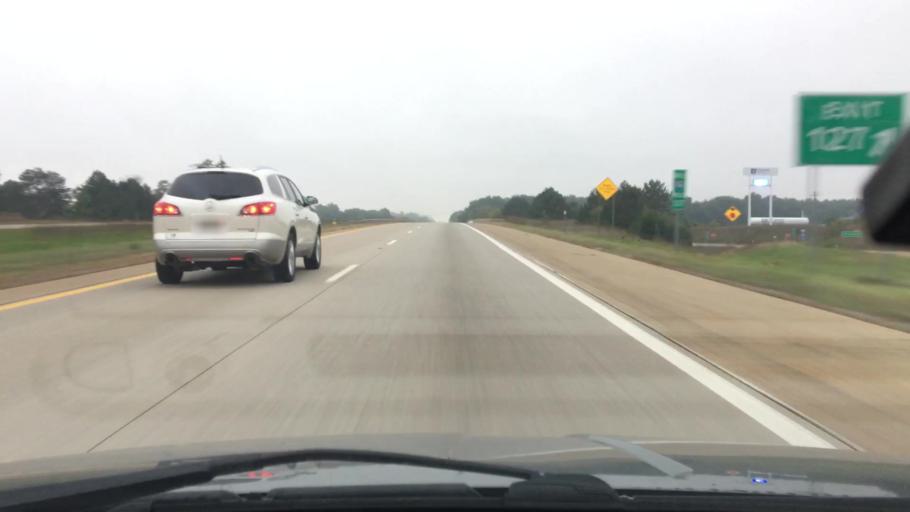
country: US
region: Michigan
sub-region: Jackson County
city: Concord
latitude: 42.2623
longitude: -84.6469
